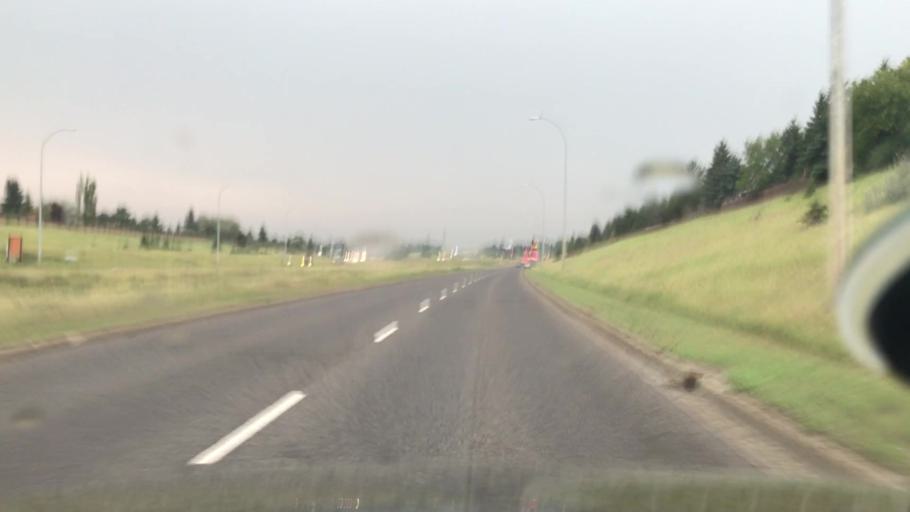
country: CA
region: Alberta
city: Edmonton
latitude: 53.4733
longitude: -113.5779
